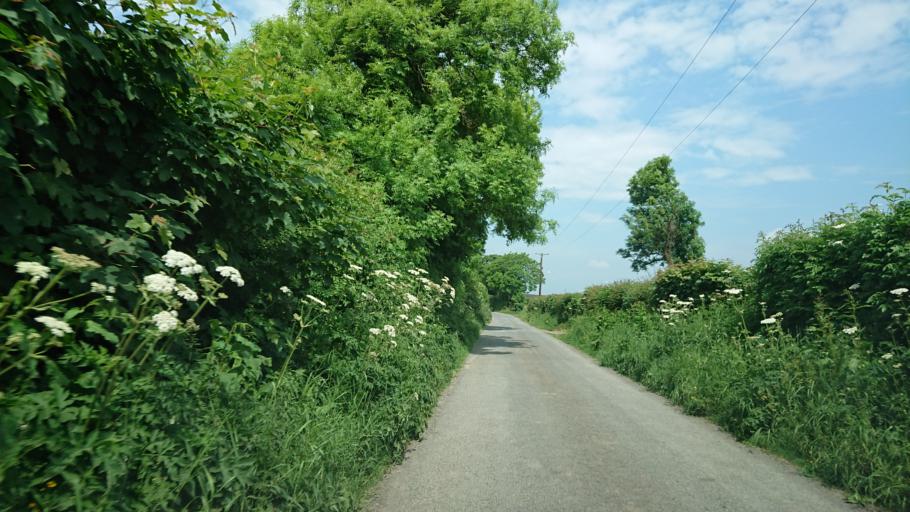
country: IE
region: Munster
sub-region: Waterford
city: Dunmore East
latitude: 52.2200
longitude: -7.0021
